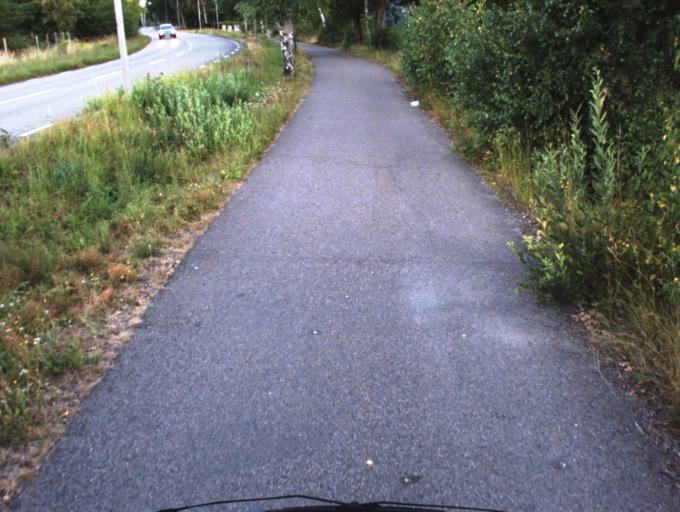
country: SE
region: Skane
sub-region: Helsingborg
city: Helsingborg
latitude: 56.0742
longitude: 12.6922
